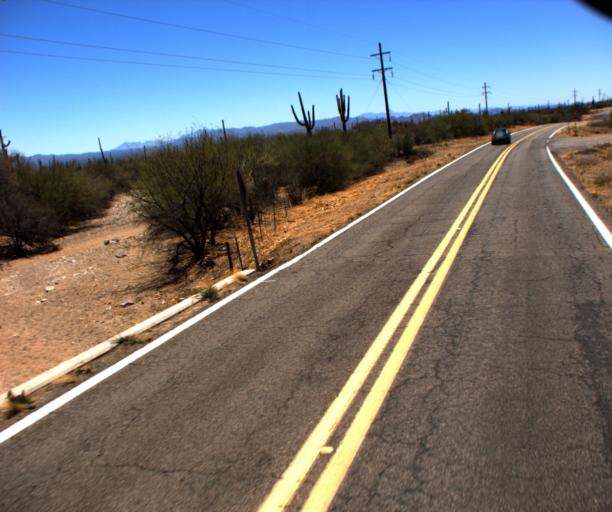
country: US
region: Arizona
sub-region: Pima County
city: Sells
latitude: 32.1569
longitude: -112.1088
